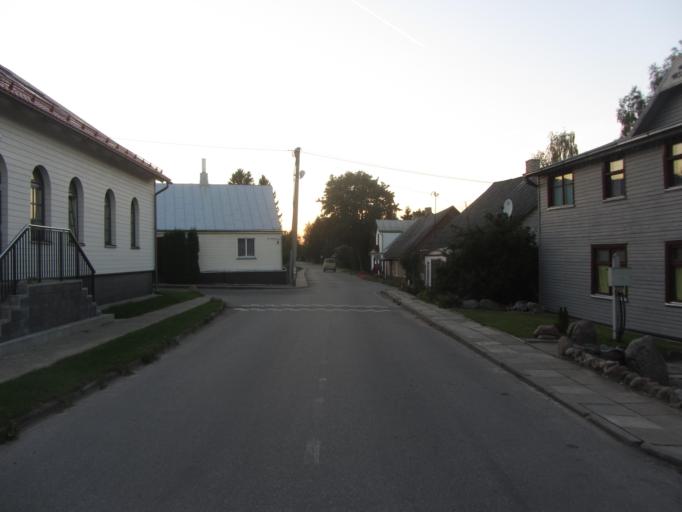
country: LT
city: Sakiai
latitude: 55.0788
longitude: 23.2732
